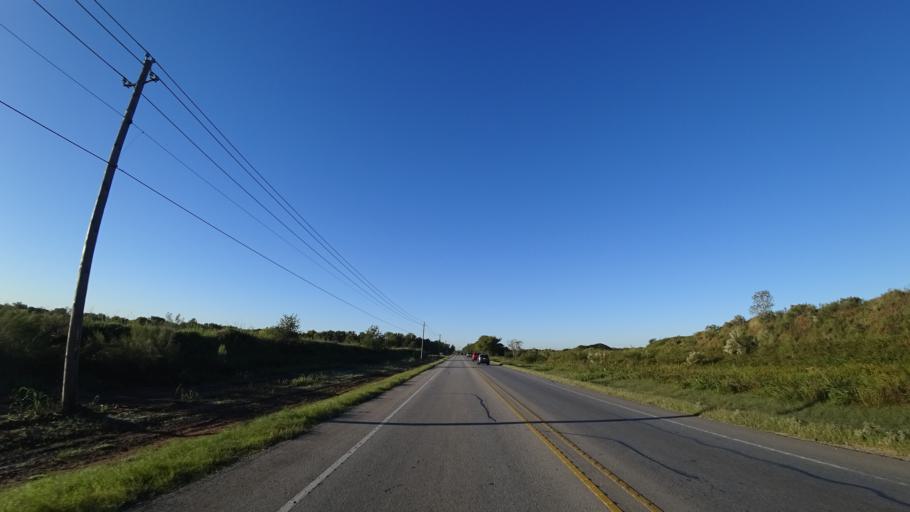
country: US
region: Texas
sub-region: Travis County
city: Hornsby Bend
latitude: 30.2293
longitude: -97.6294
